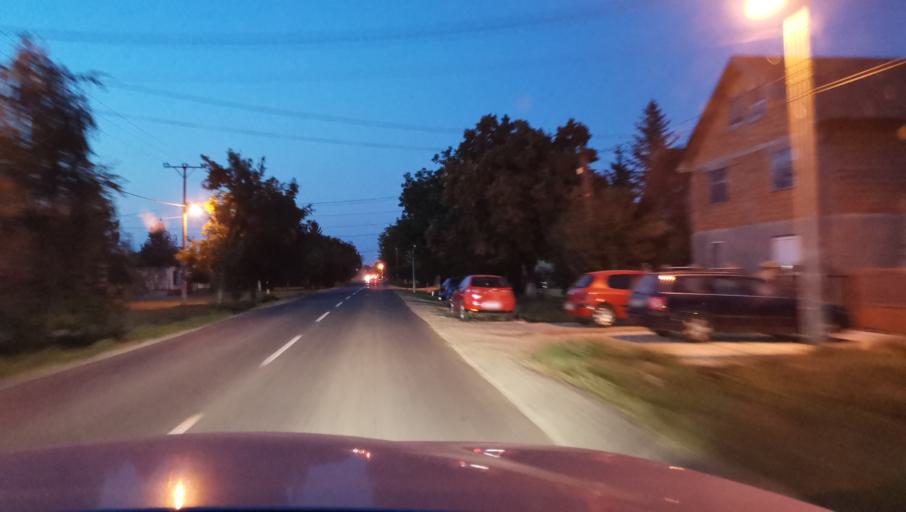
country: RS
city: Boljevci
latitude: 44.7481
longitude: 20.2552
